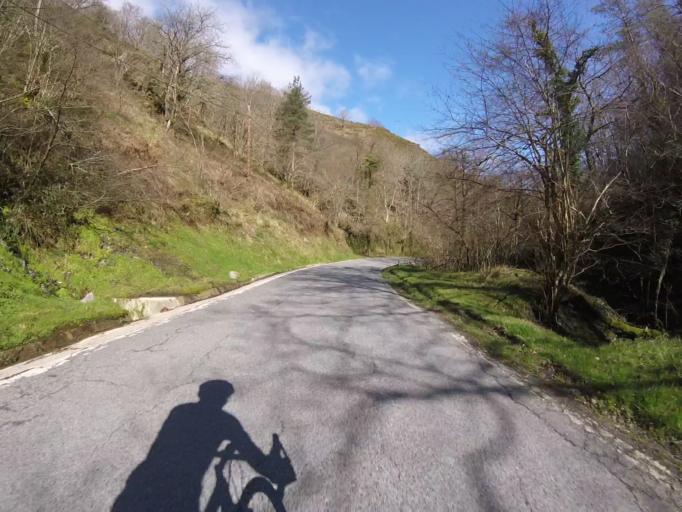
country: ES
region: Navarre
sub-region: Provincia de Navarra
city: Ezkurra
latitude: 43.0948
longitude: -1.8655
